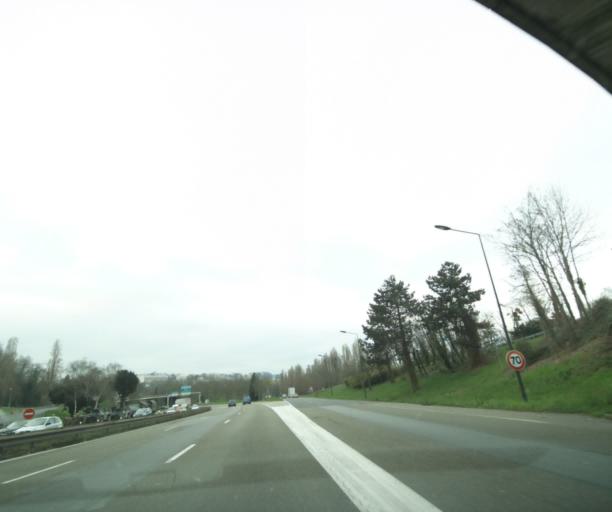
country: FR
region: Ile-de-France
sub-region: Departement des Yvelines
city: Le Port-Marly
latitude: 48.8847
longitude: 2.1061
